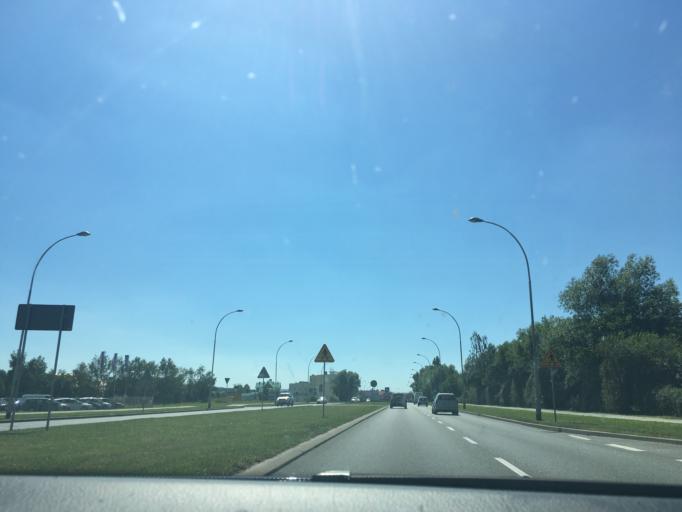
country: PL
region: Subcarpathian Voivodeship
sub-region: Rzeszow
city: Rzeszow
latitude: 50.0230
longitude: 22.0293
